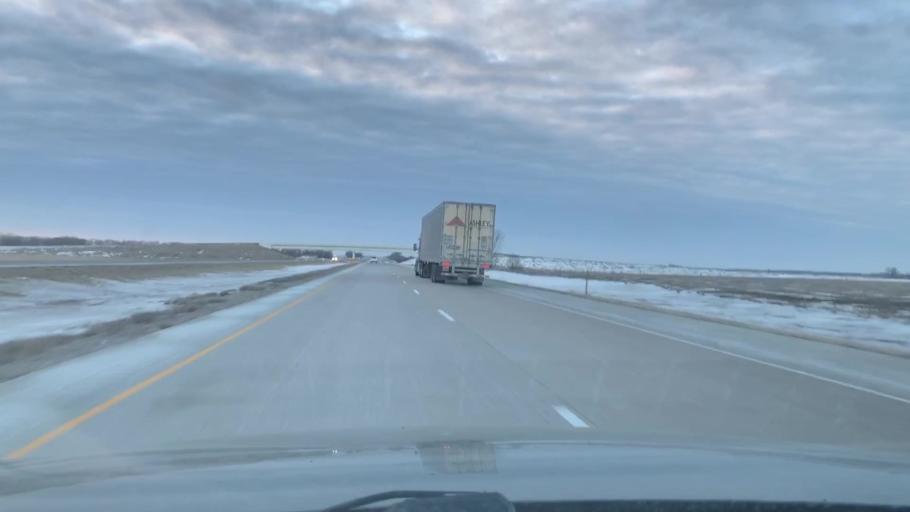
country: US
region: North Dakota
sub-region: Barnes County
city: Valley City
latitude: 46.9197
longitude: -97.7198
